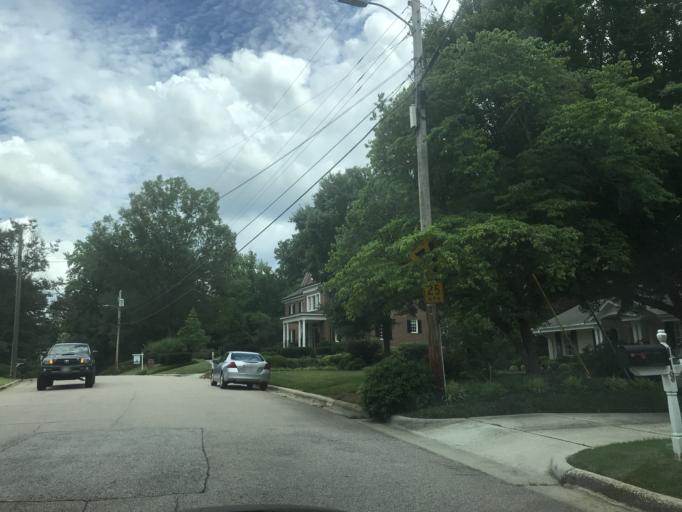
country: US
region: North Carolina
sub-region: Wake County
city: West Raleigh
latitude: 35.8243
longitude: -78.6434
